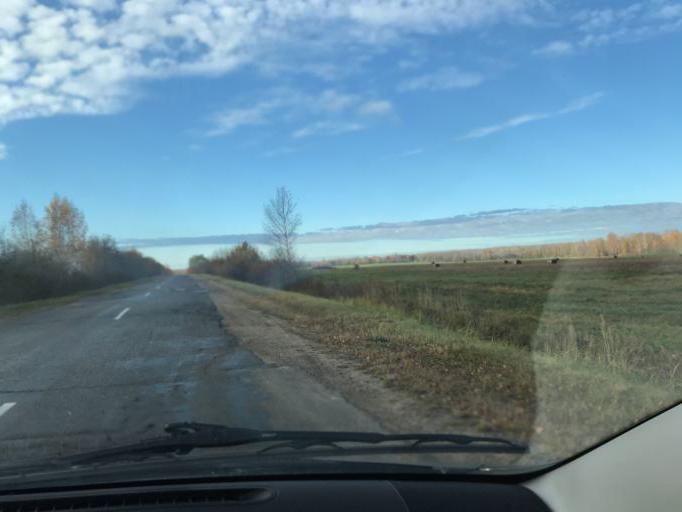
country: BY
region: Vitebsk
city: Haradok
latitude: 55.4079
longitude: 29.7448
